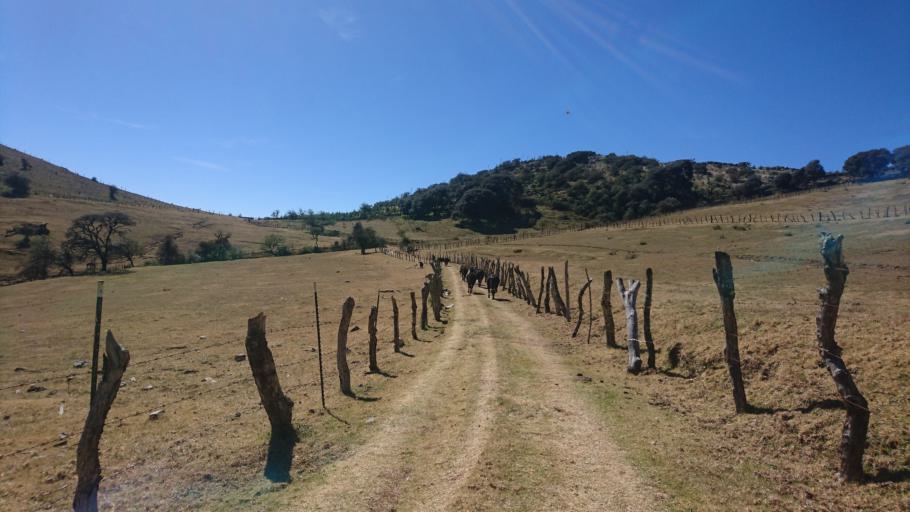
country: MX
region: San Luis Potosi
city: Zaragoza
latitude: 22.0214
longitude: -100.6204
